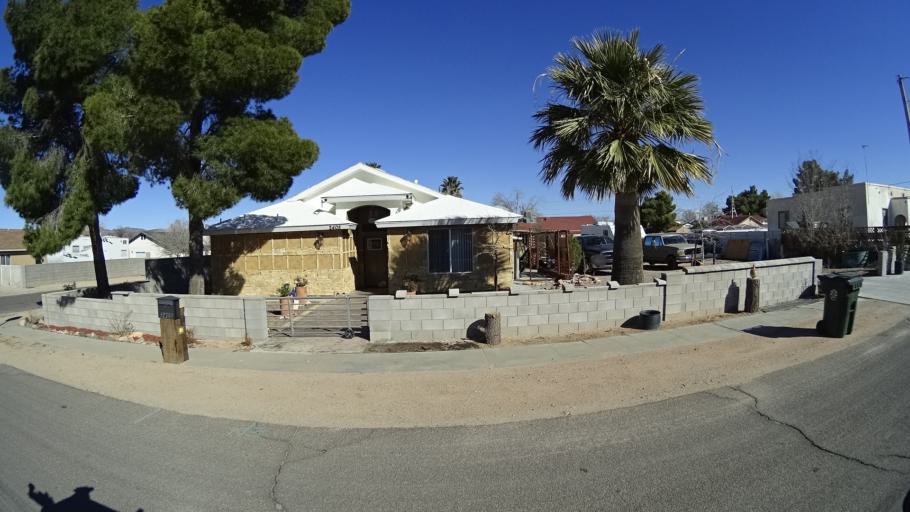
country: US
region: Arizona
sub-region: Mohave County
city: Kingman
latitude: 35.1966
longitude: -114.0221
